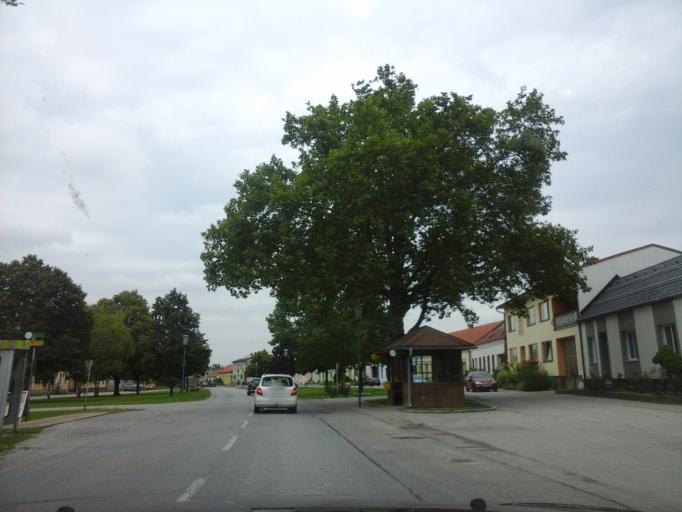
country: AT
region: Lower Austria
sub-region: Politischer Bezirk Ganserndorf
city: Eckartsau
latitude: 48.1644
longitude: 16.7821
